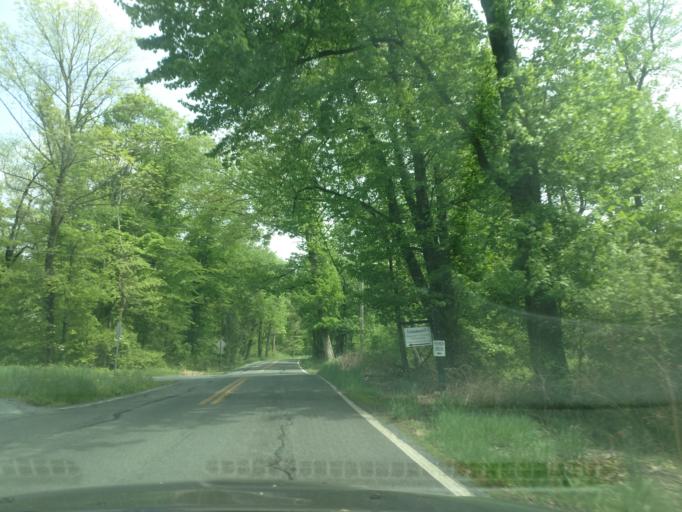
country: US
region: Pennsylvania
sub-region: Chester County
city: Elverson
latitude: 40.1735
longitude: -75.8518
